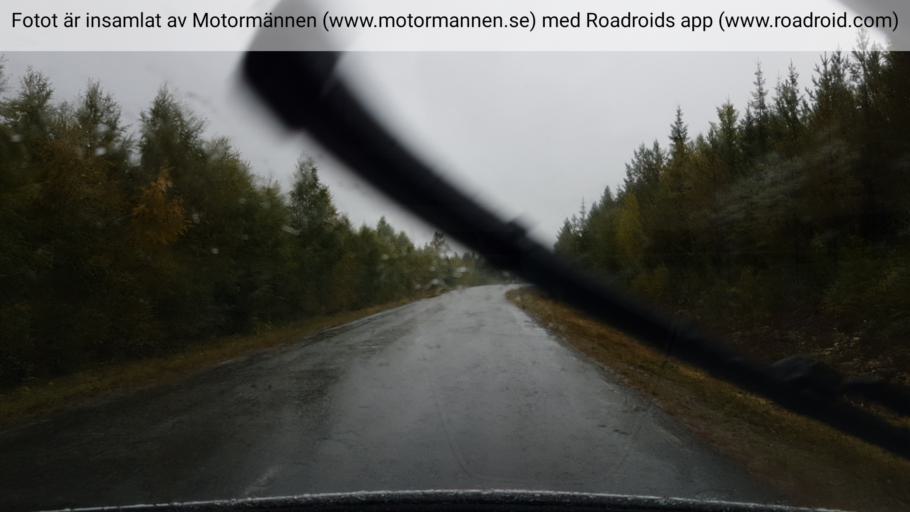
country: SE
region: Vaesterbotten
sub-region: Vannas Kommun
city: Vannasby
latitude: 64.0388
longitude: 19.9315
